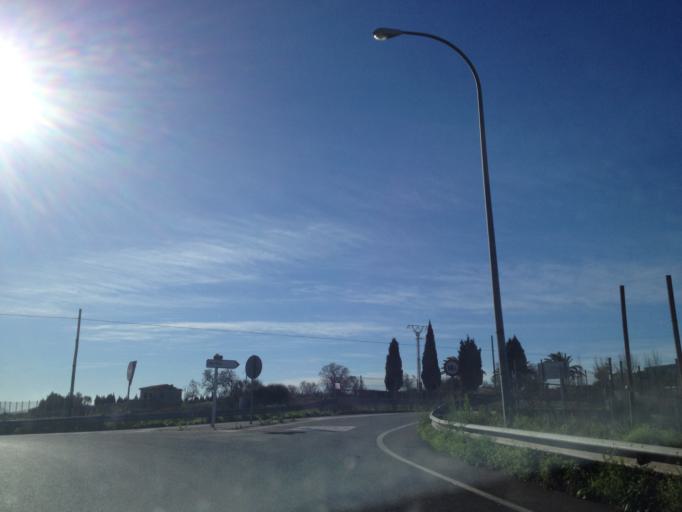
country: ES
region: Balearic Islands
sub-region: Illes Balears
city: Petra
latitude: 39.6172
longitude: 3.1216
